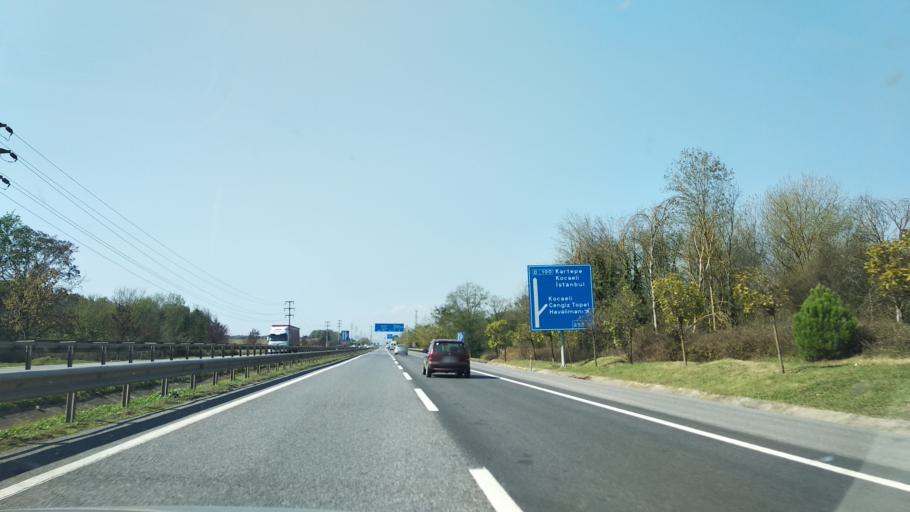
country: TR
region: Kocaeli
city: Derbent
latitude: 40.7422
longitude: 30.0866
